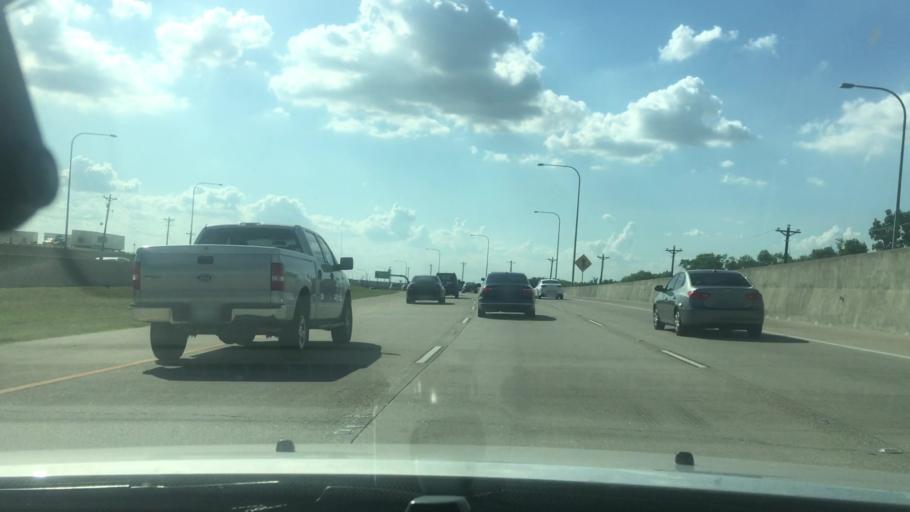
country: US
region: Texas
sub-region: Collin County
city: Frisco
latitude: 33.1342
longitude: -96.8272
